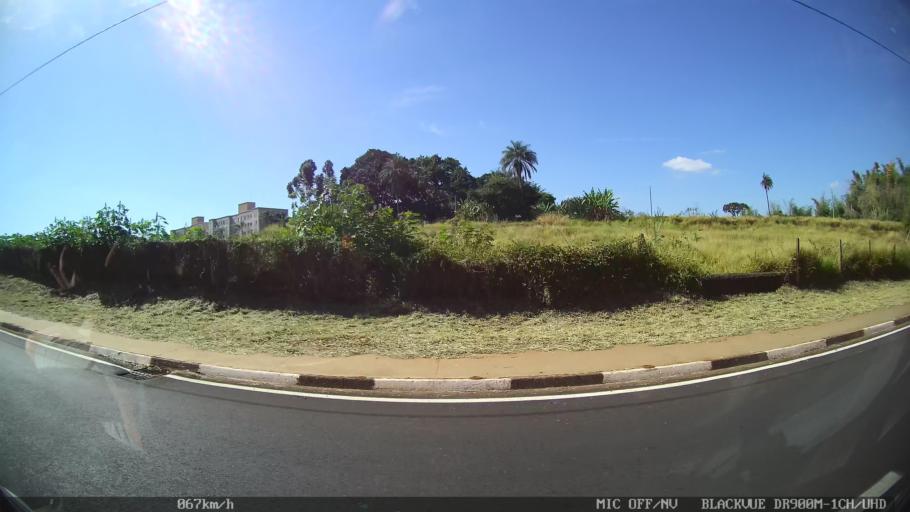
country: BR
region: Sao Paulo
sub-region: Franca
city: Franca
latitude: -20.5444
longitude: -47.4208
